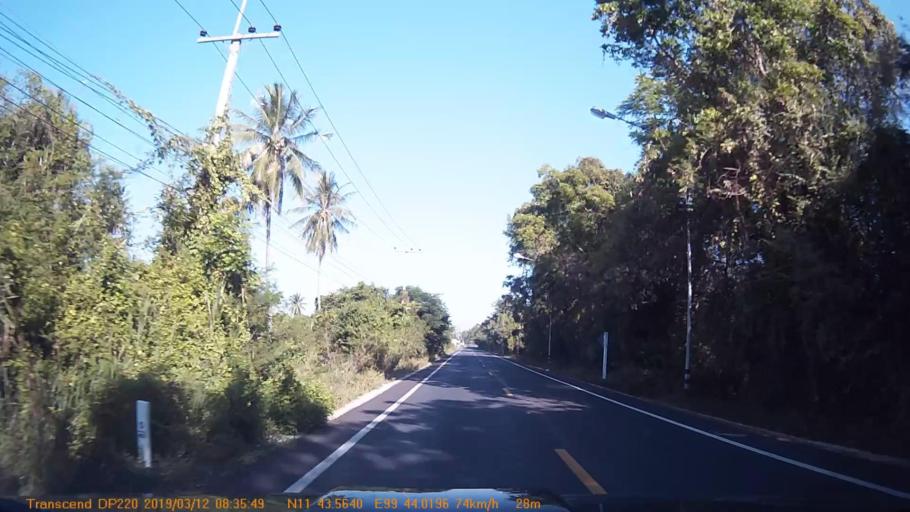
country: TH
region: Prachuap Khiri Khan
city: Prachuap Khiri Khan
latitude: 11.7263
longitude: 99.7334
